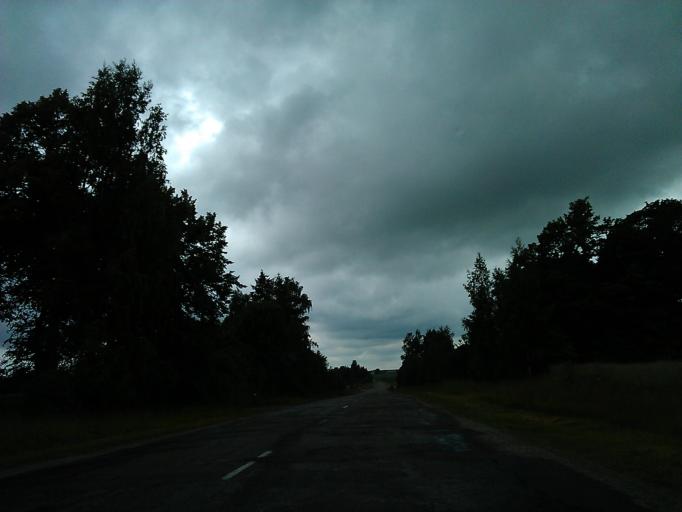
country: LV
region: Kuldigas Rajons
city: Kuldiga
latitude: 56.8472
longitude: 21.7824
